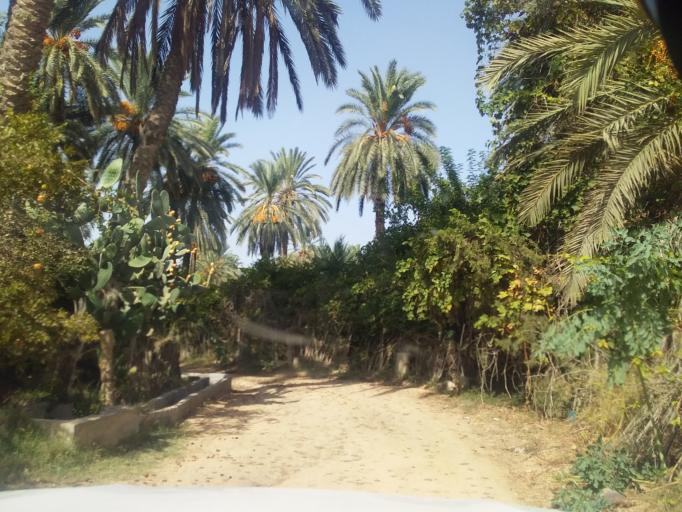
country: TN
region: Qabis
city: Gabes
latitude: 33.6265
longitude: 10.2858
